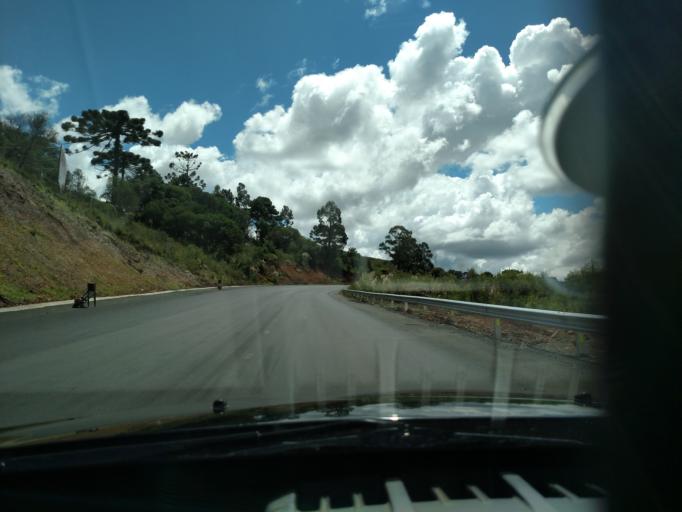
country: BR
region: Santa Catarina
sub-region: Sao Joaquim
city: Sao Joaquim
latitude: -28.2432
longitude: -49.9677
